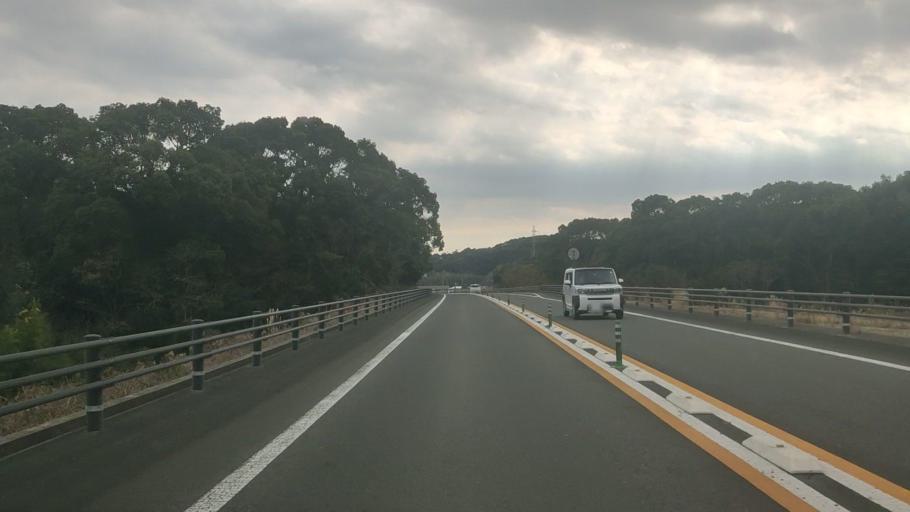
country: JP
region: Nagasaki
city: Shimabara
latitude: 32.7660
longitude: 130.3601
